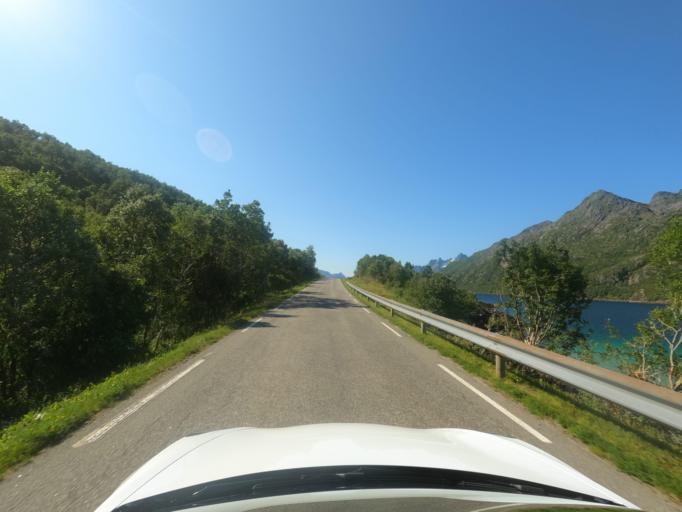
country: NO
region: Nordland
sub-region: Hadsel
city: Stokmarknes
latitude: 68.3874
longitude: 15.0953
